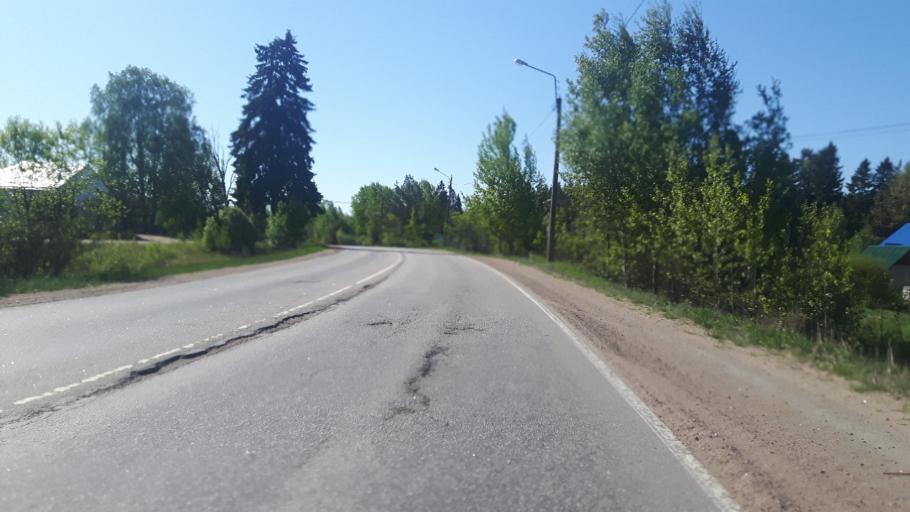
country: RU
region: Leningrad
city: Vyborg
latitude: 60.6527
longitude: 28.7444
